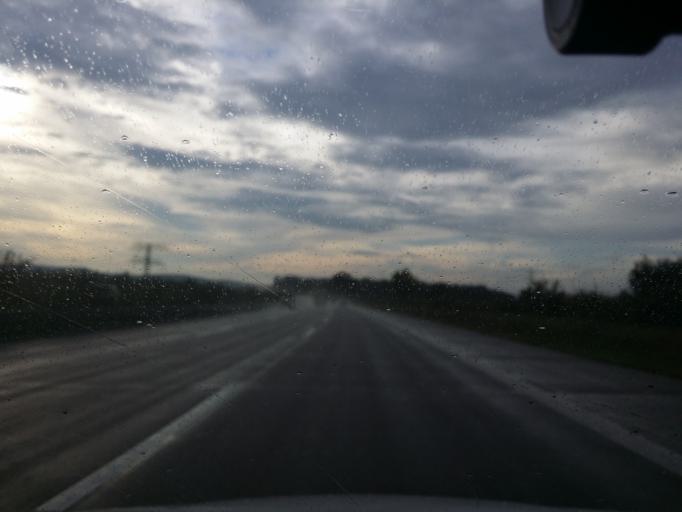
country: DE
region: Thuringia
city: Horselgau
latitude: 50.9191
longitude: 10.5699
